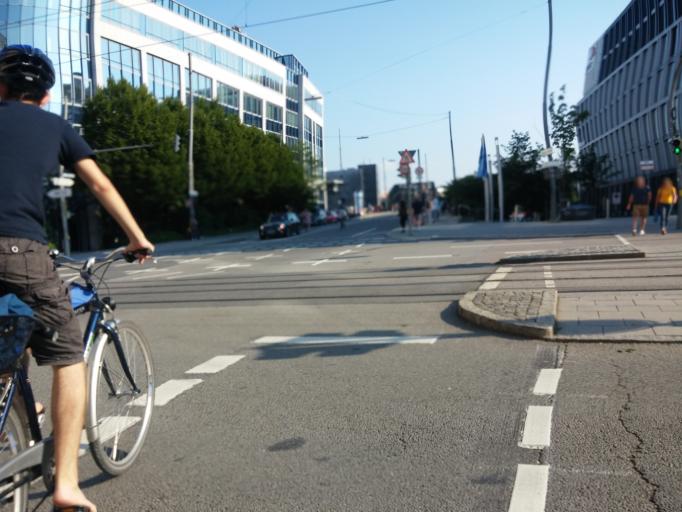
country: DE
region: Bavaria
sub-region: Upper Bavaria
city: Munich
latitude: 48.1438
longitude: 11.5488
